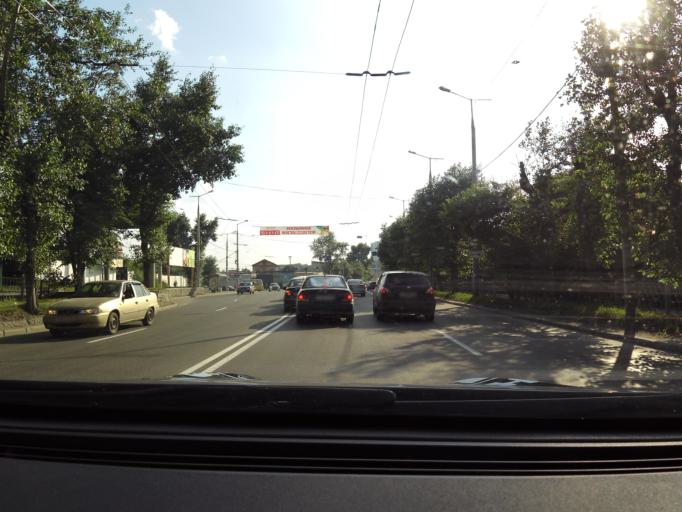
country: RU
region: Sverdlovsk
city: Yekaterinburg
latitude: 56.8285
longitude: 60.5687
